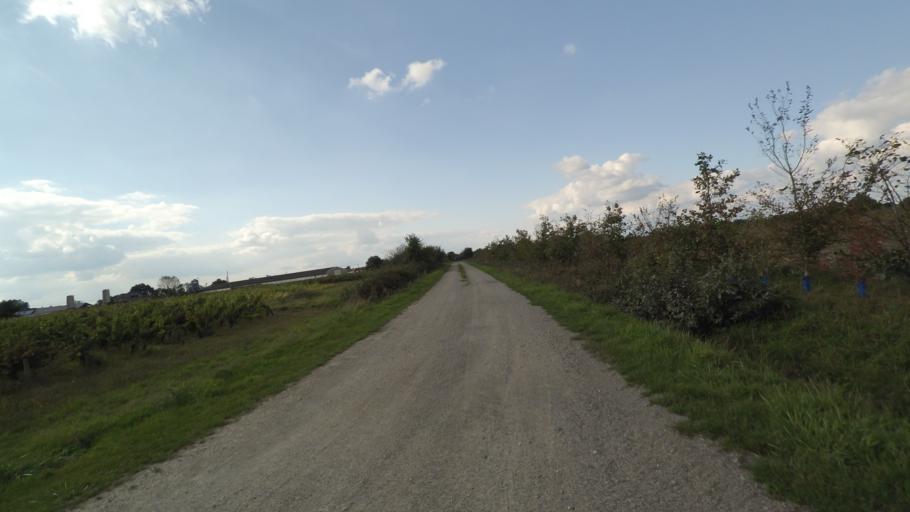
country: FR
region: Pays de la Loire
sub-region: Departement de la Loire-Atlantique
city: Vieillevigne
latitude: 46.9765
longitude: -1.4057
